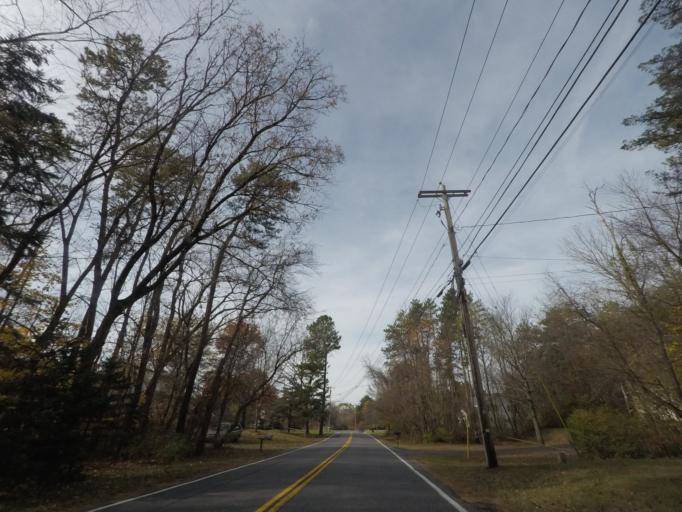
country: US
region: New York
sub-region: Albany County
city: Westmere
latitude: 42.7229
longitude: -73.8817
